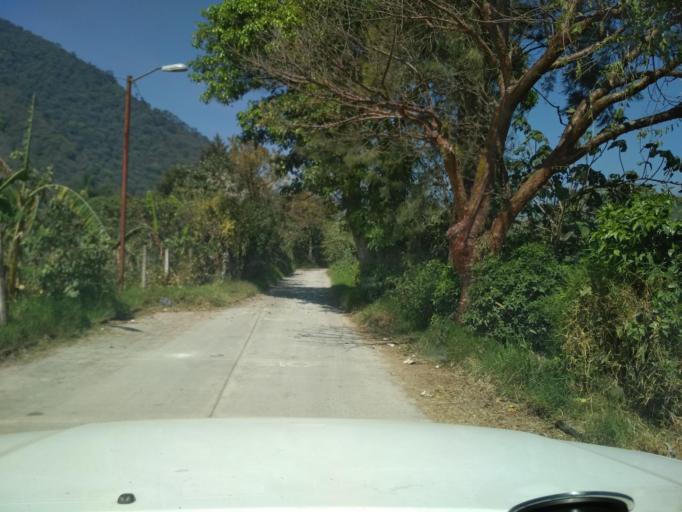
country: MX
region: Veracruz
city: Jalapilla
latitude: 18.8208
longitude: -97.0917
